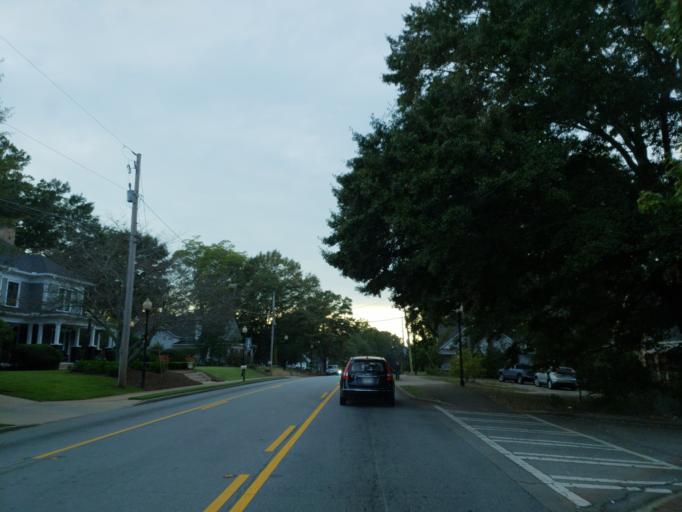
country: US
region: Georgia
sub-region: Cobb County
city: Powder Springs
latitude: 33.8588
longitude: -84.6762
